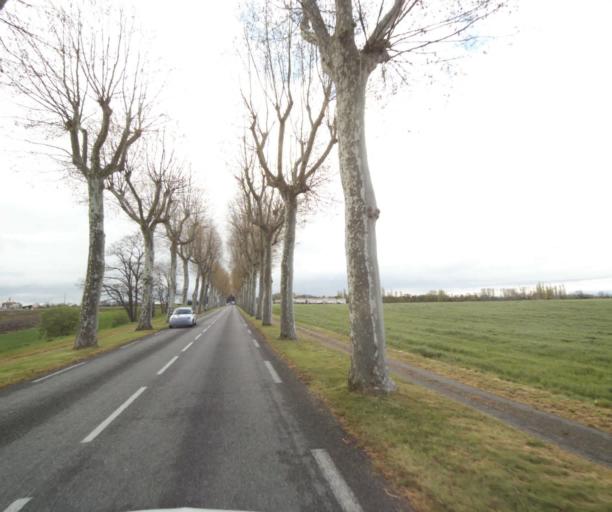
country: FR
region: Midi-Pyrenees
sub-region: Departement de l'Ariege
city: Saverdun
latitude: 43.2315
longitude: 1.5905
